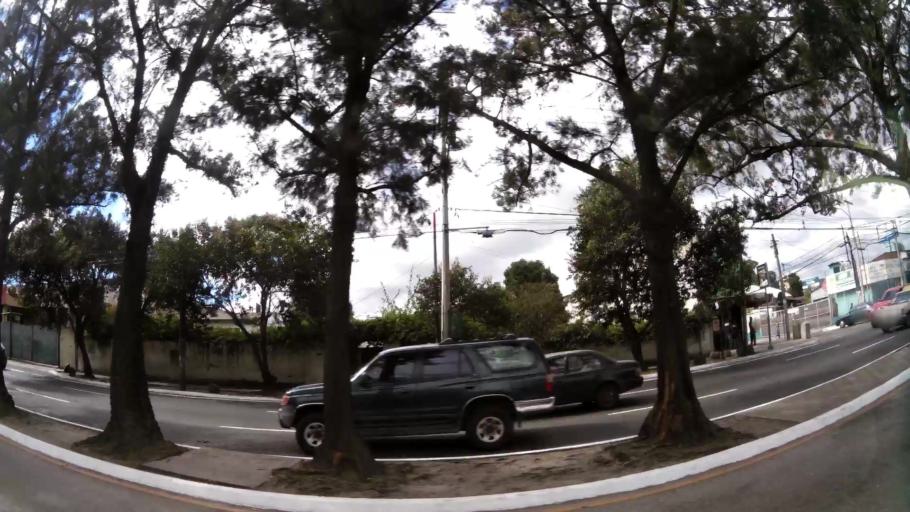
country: GT
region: Guatemala
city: Guatemala City
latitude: 14.6214
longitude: -90.5460
